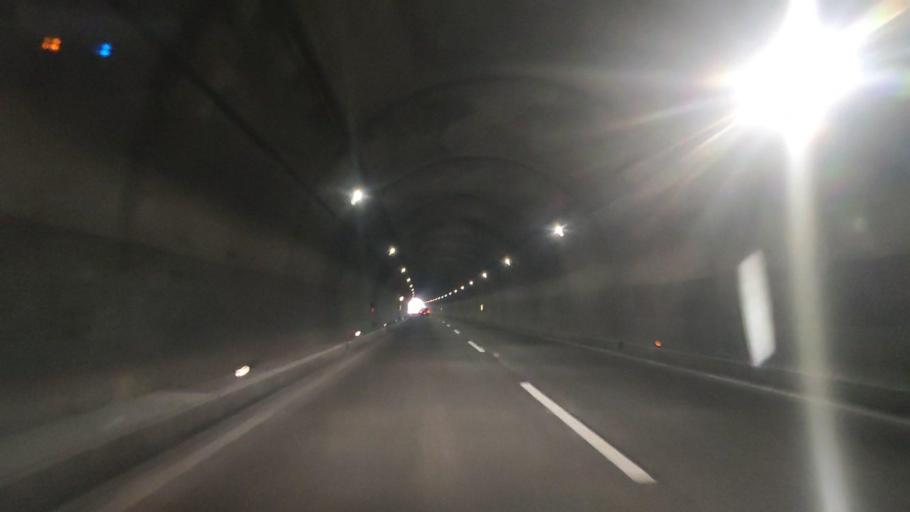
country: JP
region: Oita
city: Beppu
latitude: 33.2757
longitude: 131.3434
